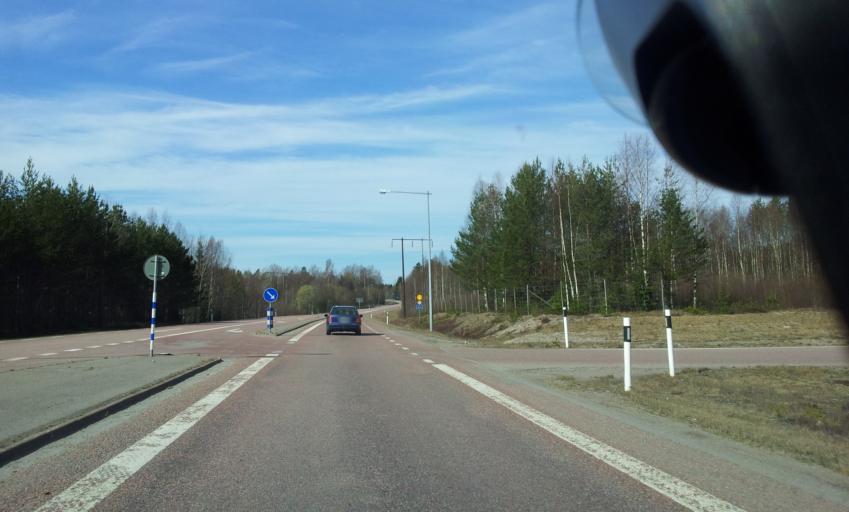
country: SE
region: Gaevleborg
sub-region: Hudiksvalls Kommun
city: Hudiksvall
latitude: 61.7139
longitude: 17.0716
